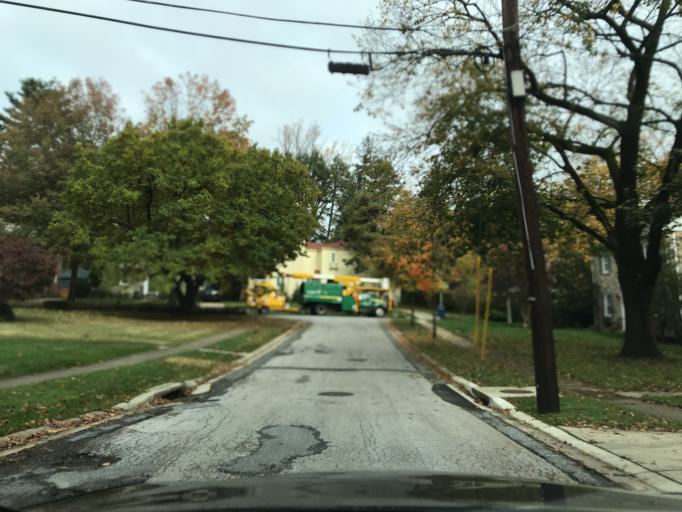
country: US
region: Maryland
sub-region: Baltimore County
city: Towson
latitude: 39.3823
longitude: -76.6028
